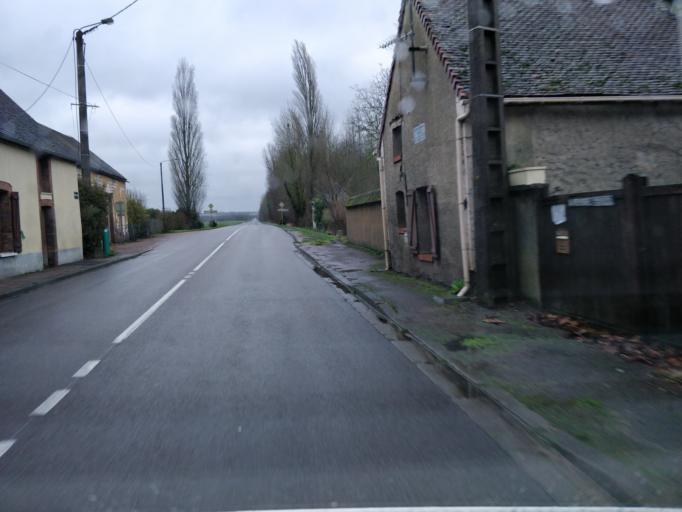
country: FR
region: Bourgogne
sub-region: Departement de l'Yonne
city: Thorigny-sur-Oreuse
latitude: 48.2260
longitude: 3.5088
